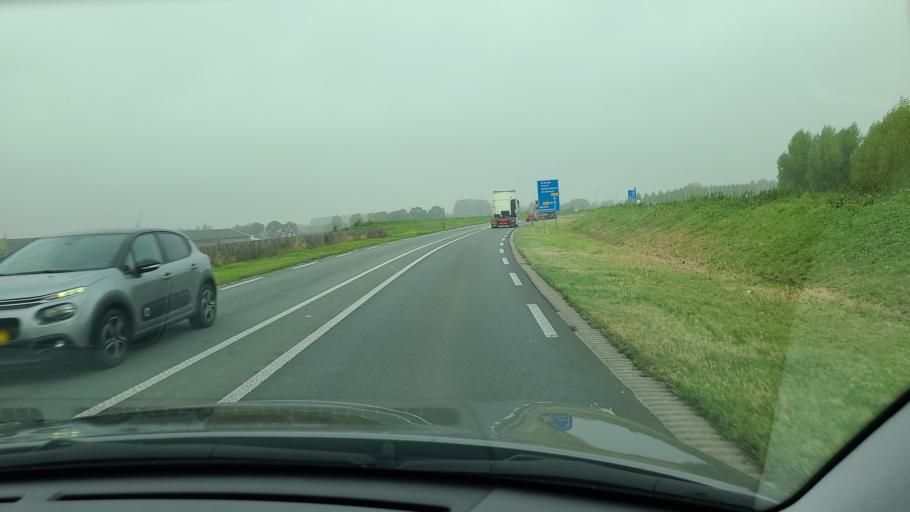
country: NL
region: Gelderland
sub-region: Gemeente Tiel
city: Tiel
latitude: 51.8719
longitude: 5.4986
